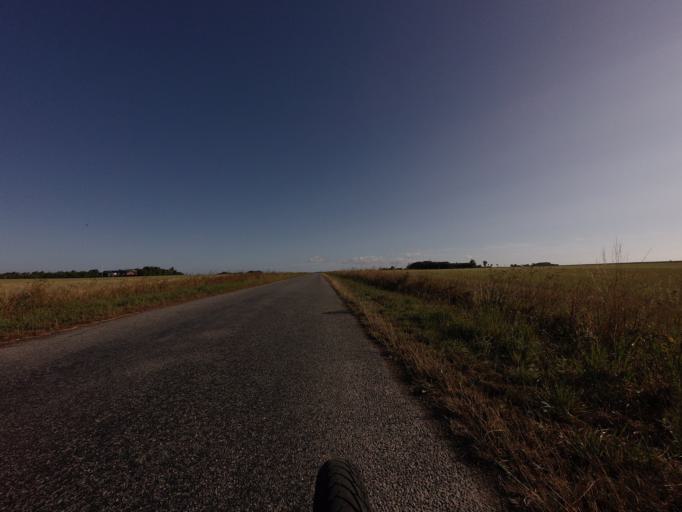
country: DK
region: North Denmark
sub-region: Hjorring Kommune
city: Vra
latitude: 57.3903
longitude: 9.9267
